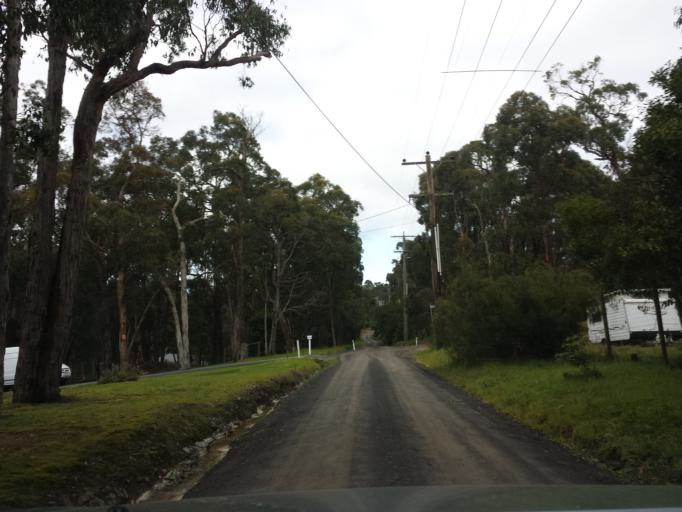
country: AU
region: Victoria
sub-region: Yarra Ranges
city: Belgrave South
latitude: -37.9282
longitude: 145.3440
